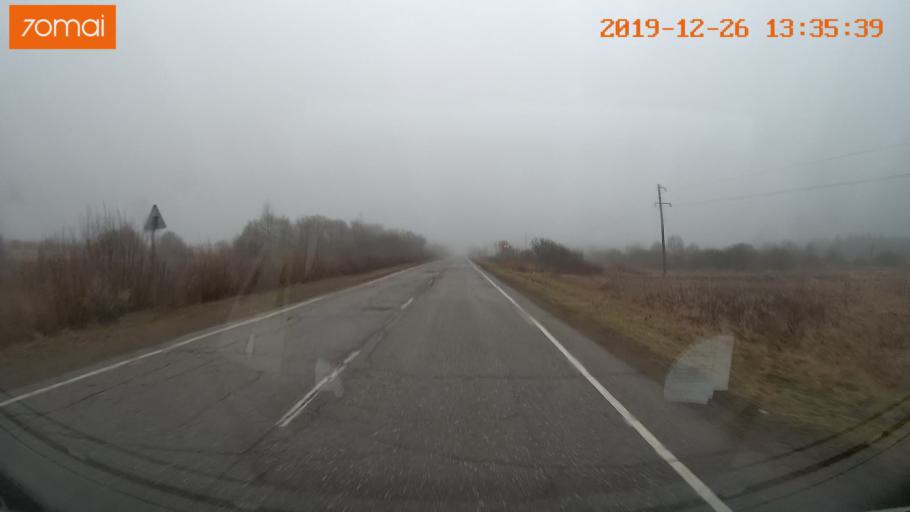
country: RU
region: Vologda
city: Sheksna
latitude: 58.7925
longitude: 38.3417
